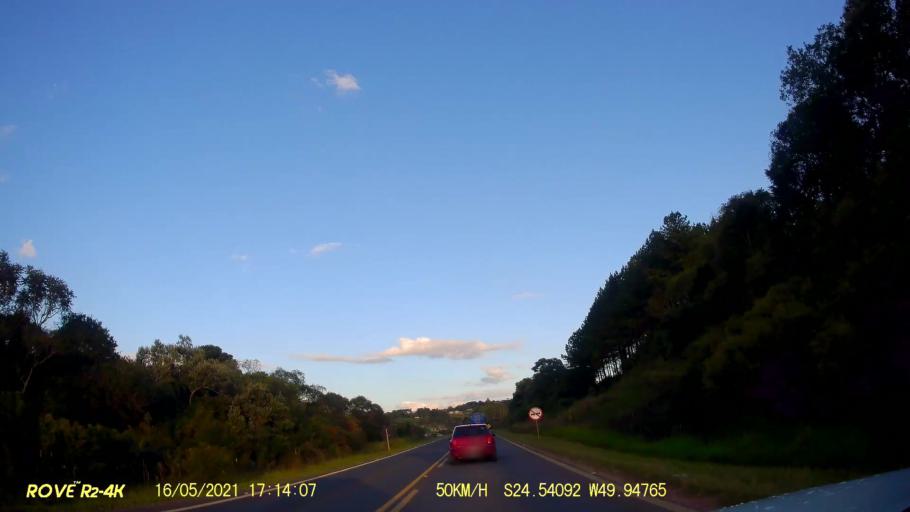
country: BR
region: Parana
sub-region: Pirai Do Sul
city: Pirai do Sul
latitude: -24.5410
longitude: -49.9475
